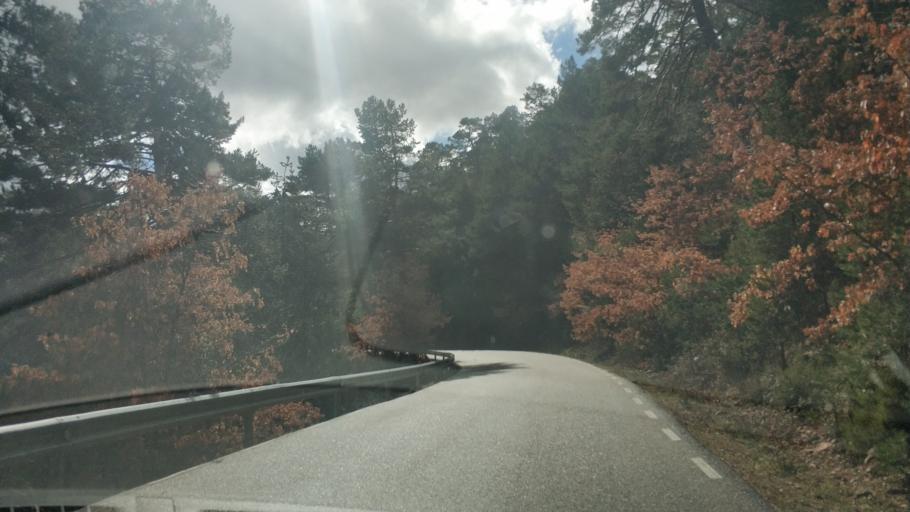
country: ES
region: Castille and Leon
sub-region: Provincia de Burgos
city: Quintanar de la Sierra
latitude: 42.0078
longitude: -3.0200
